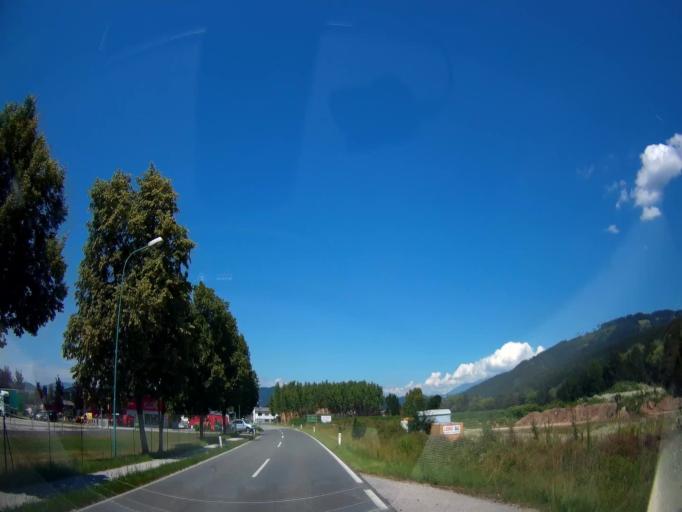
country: AT
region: Carinthia
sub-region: Politischer Bezirk Volkermarkt
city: Bleiburg/Pliberk
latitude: 46.5977
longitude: 14.7973
